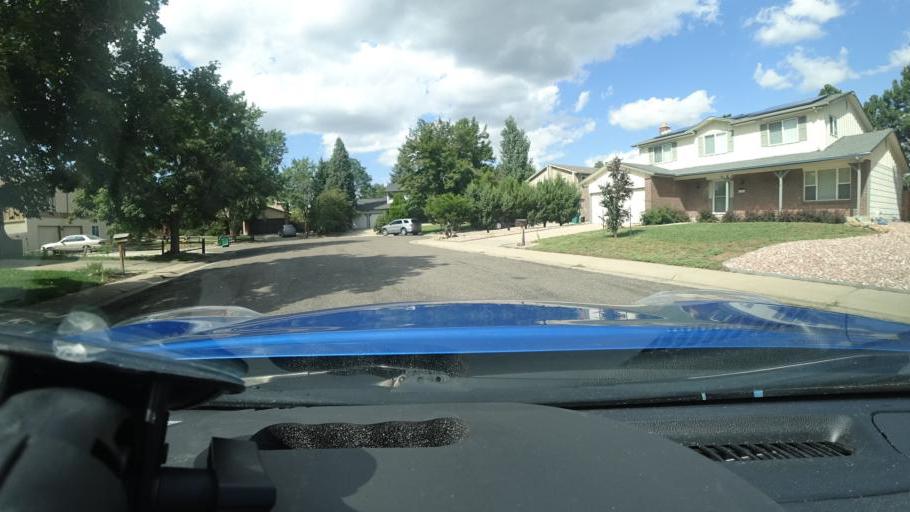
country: US
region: Colorado
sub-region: Adams County
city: Aurora
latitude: 39.6884
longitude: -104.8530
